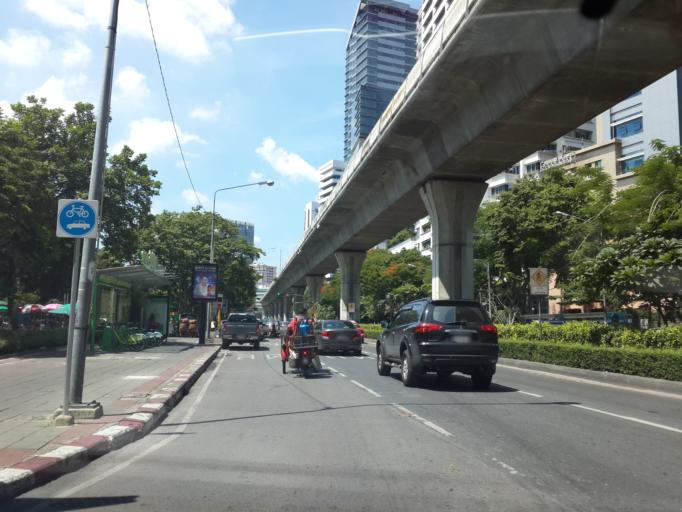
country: TH
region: Bangkok
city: Pathum Wan
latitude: 13.7342
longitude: 100.5386
